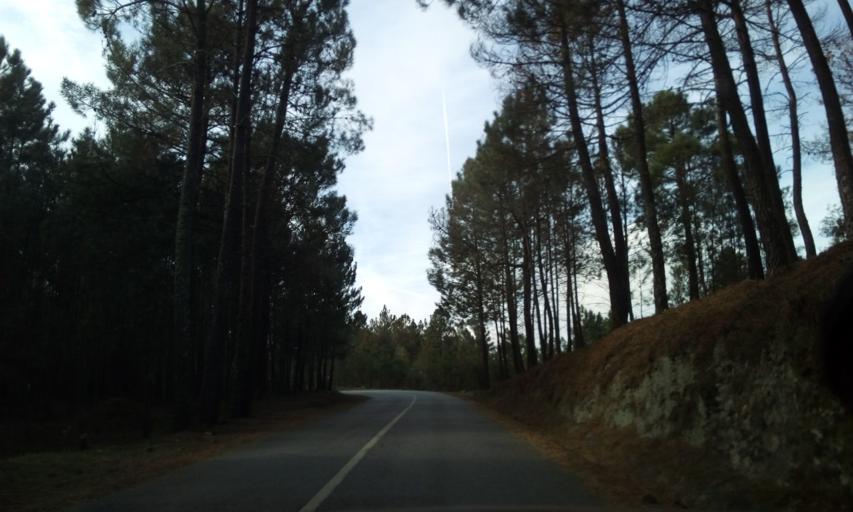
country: PT
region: Guarda
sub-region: Fornos de Algodres
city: Fornos de Algodres
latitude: 40.6920
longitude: -7.5597
